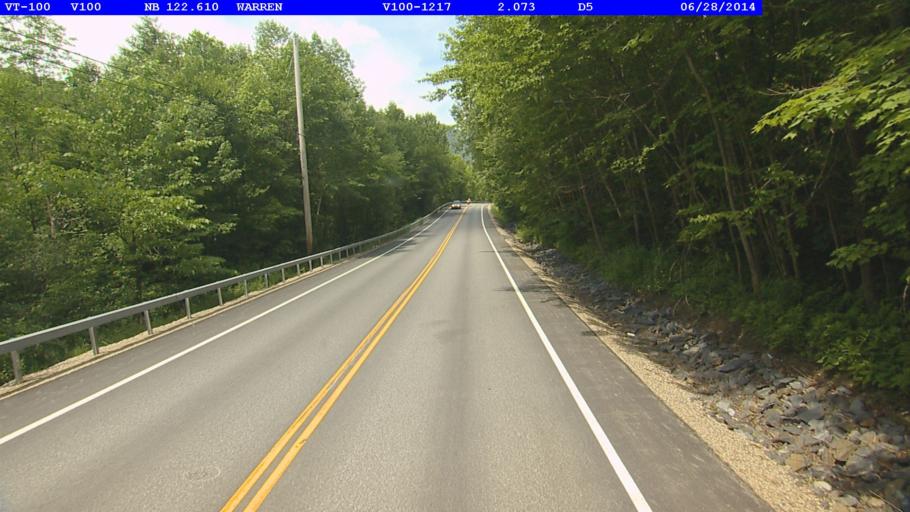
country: US
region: Vermont
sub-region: Washington County
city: Northfield
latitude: 44.0888
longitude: -72.8626
